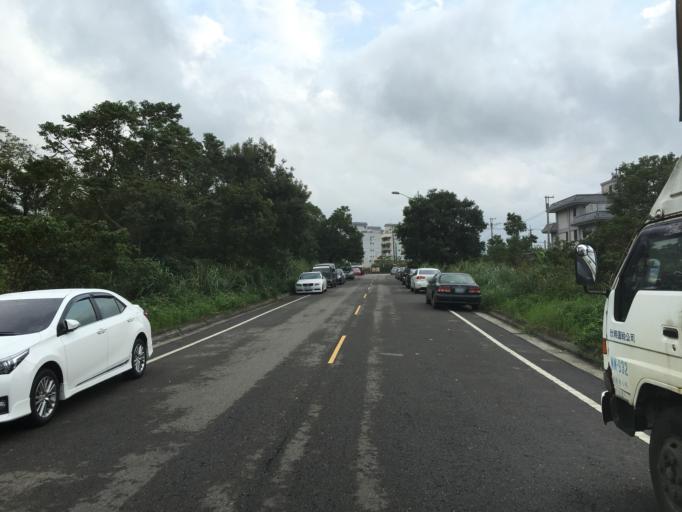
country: TW
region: Taiwan
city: Daxi
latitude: 24.8700
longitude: 121.2310
